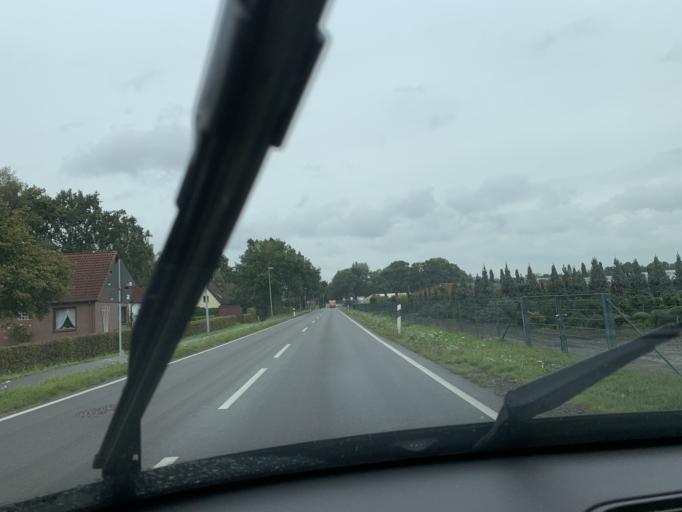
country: DE
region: Lower Saxony
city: Bad Zwischenahn
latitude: 53.1675
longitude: 8.0666
